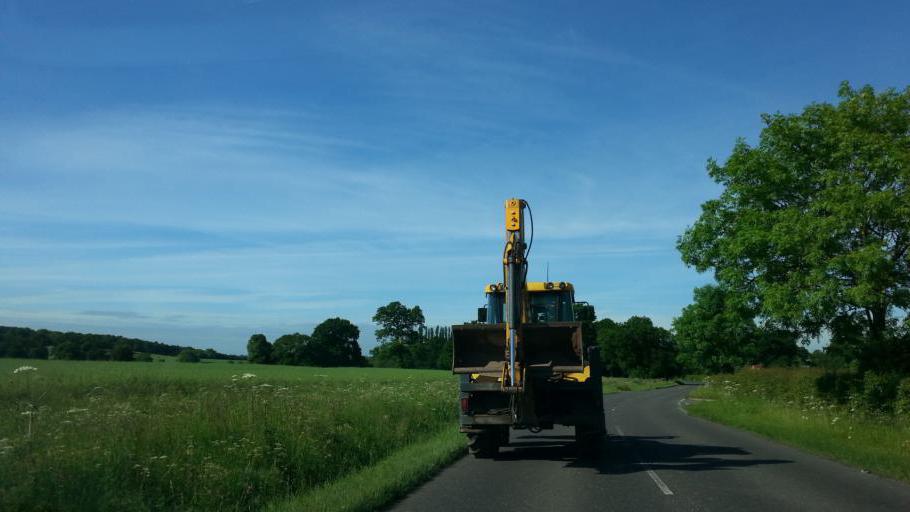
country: GB
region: England
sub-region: Nottinghamshire
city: Farnsfield
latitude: 53.0573
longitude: -1.0526
